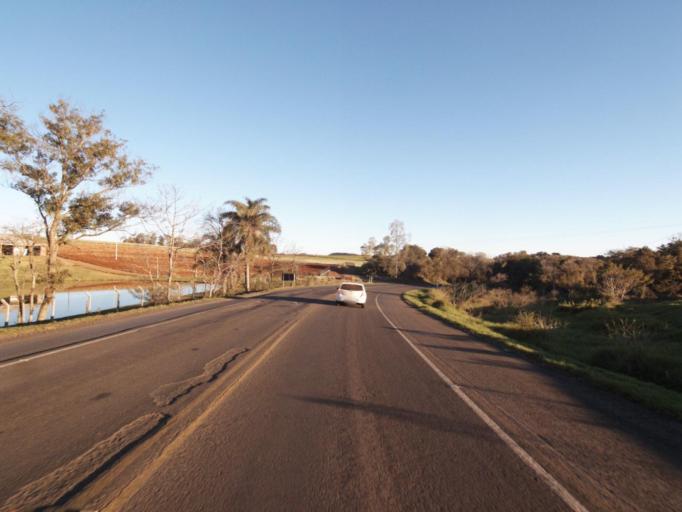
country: BR
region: Santa Catarina
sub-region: Chapeco
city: Chapeco
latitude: -26.8302
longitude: -53.0097
